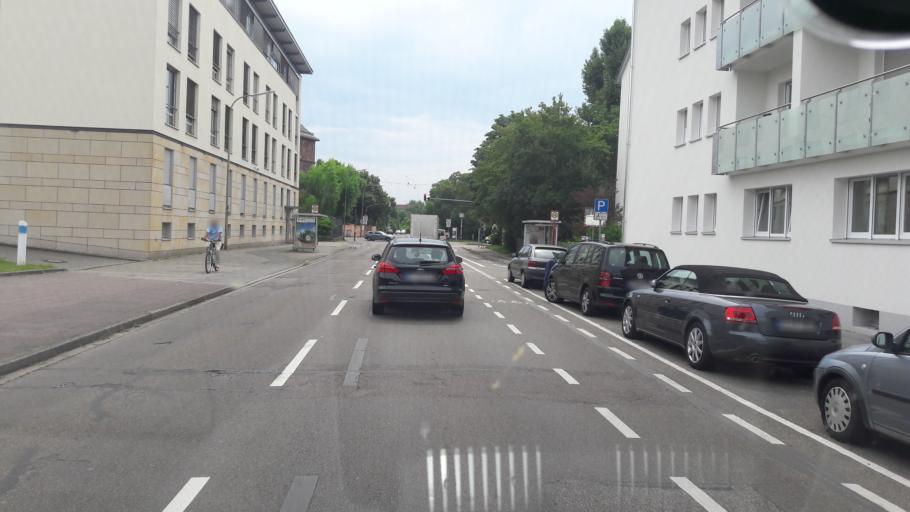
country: DE
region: Baden-Wuerttemberg
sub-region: Karlsruhe Region
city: Karlsruhe
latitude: 49.0206
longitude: 8.3654
